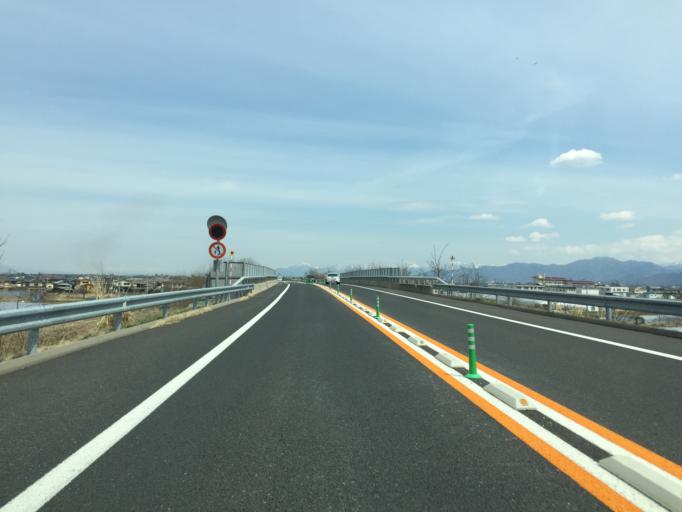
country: JP
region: Yamagata
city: Yamagata-shi
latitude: 38.2543
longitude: 140.2871
